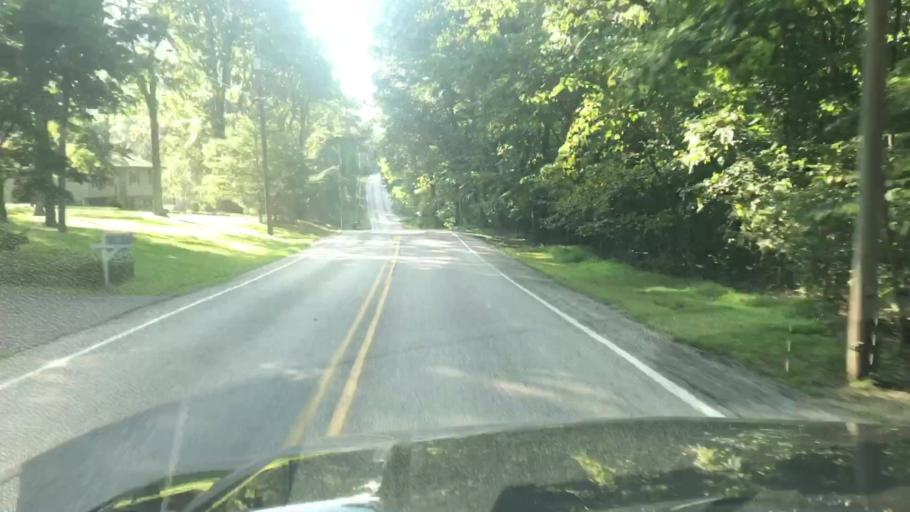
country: US
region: Pennsylvania
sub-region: York County
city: Valley Green
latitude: 40.1555
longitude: -76.8494
